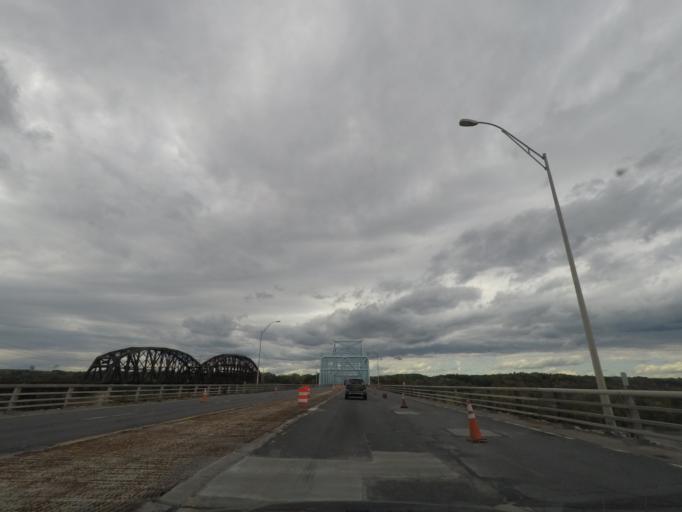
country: US
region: New York
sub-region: Rensselaer County
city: Castleton-on-Hudson
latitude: 42.5084
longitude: -73.7698
